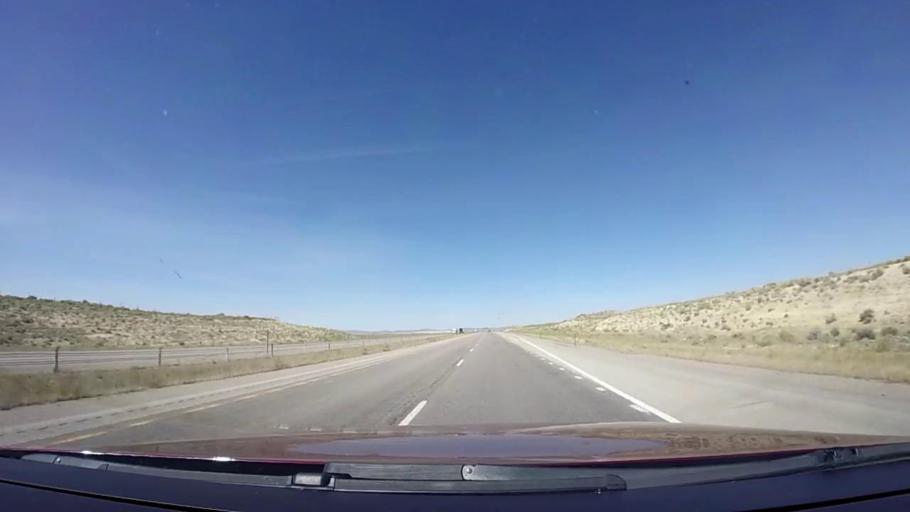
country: US
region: Wyoming
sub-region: Sweetwater County
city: Rock Springs
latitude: 41.6490
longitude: -108.6254
